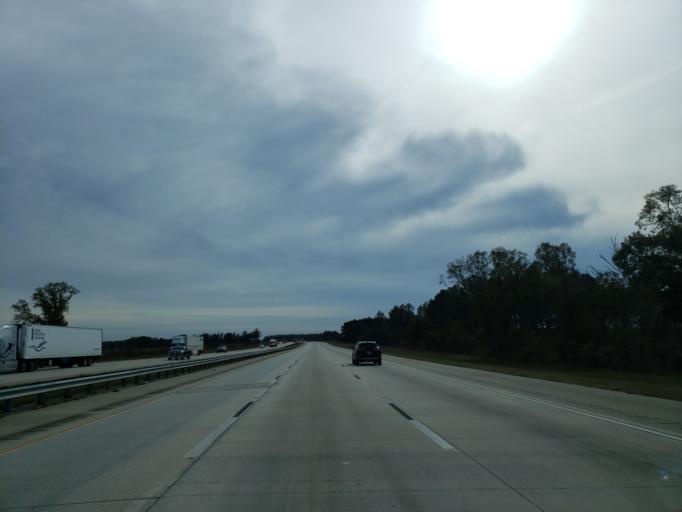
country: US
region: Georgia
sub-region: Dooly County
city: Vienna
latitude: 32.0432
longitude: -83.7629
